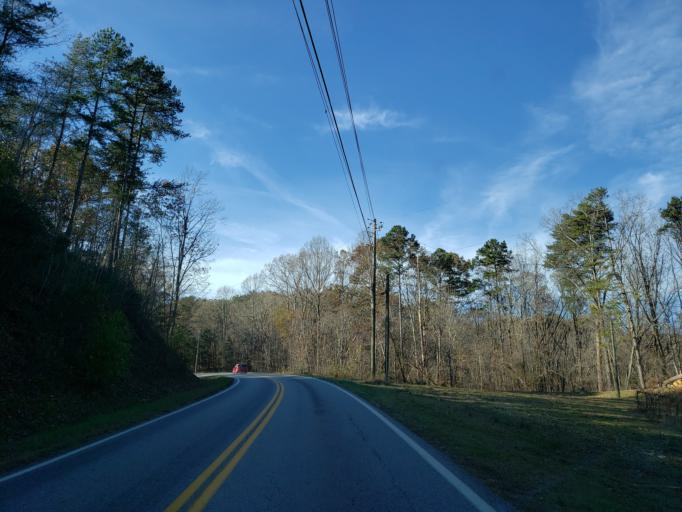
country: US
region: Georgia
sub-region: Lumpkin County
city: Dahlonega
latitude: 34.4518
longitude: -83.9938
